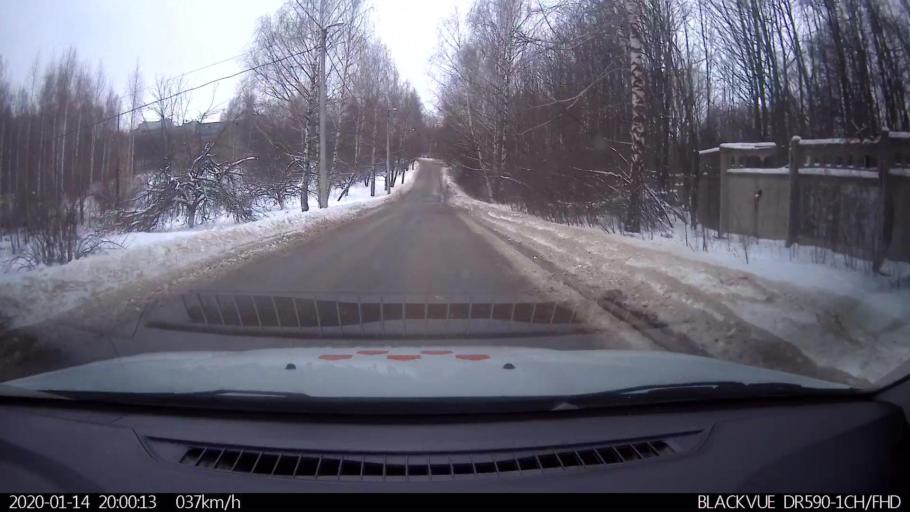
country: RU
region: Nizjnij Novgorod
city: Nizhniy Novgorod
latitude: 56.2392
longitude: 43.9423
